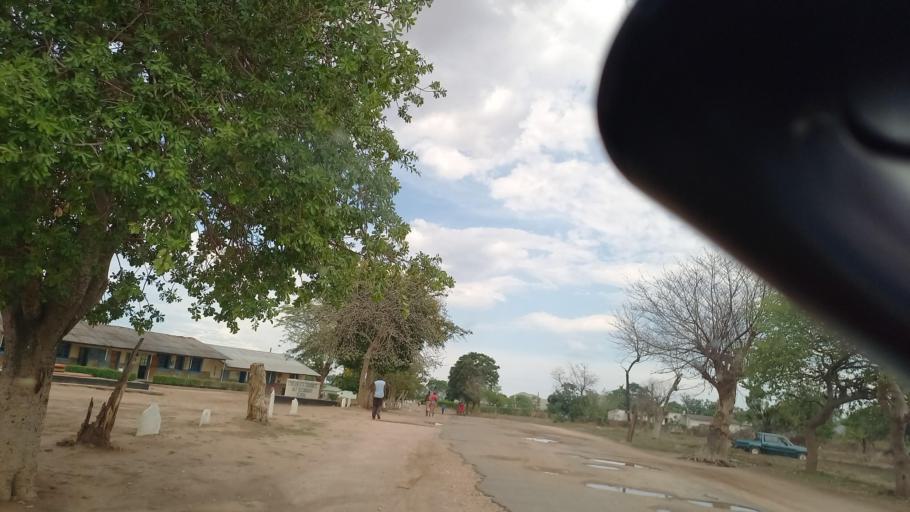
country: ZM
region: Lusaka
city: Kafue
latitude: -16.2255
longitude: 28.1326
